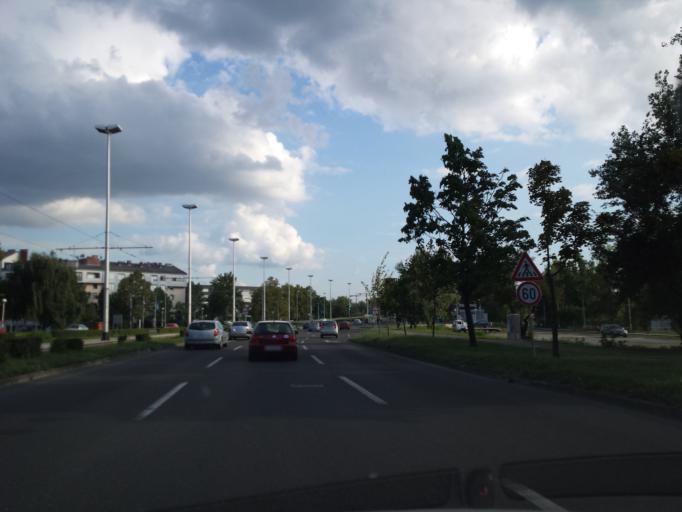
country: HR
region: Grad Zagreb
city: Novi Zagreb
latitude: 45.7899
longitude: 16.0038
